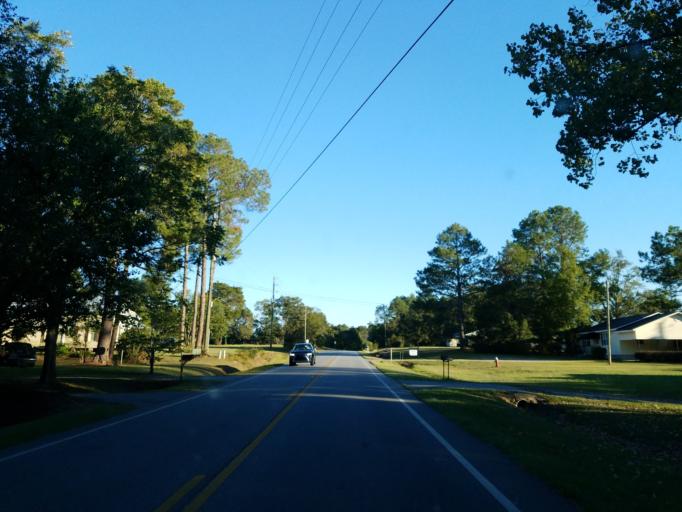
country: US
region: Georgia
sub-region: Worth County
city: Sylvester
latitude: 31.5642
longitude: -83.8517
